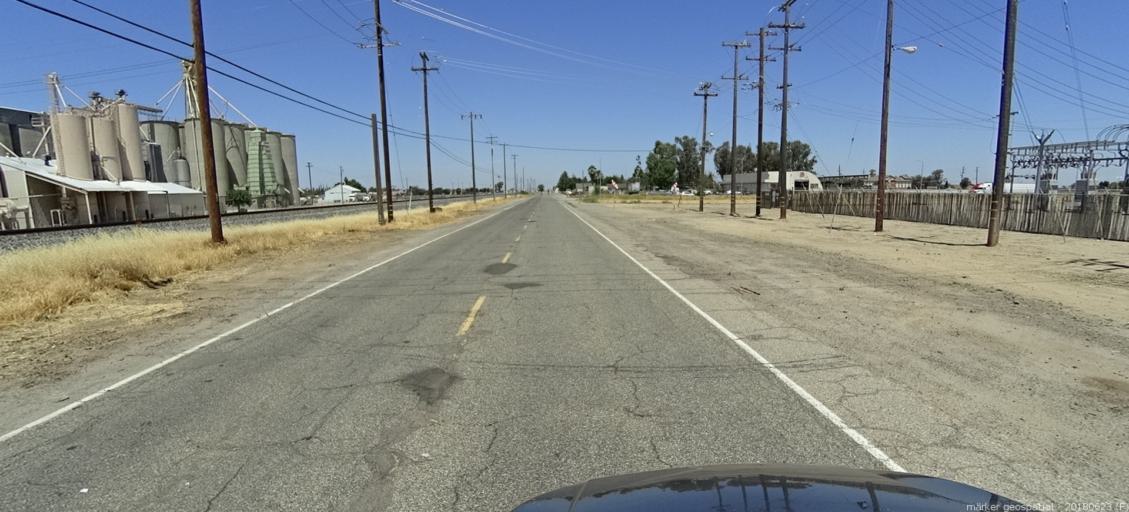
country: US
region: California
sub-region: Madera County
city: Chowchilla
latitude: 37.1202
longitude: -120.2511
